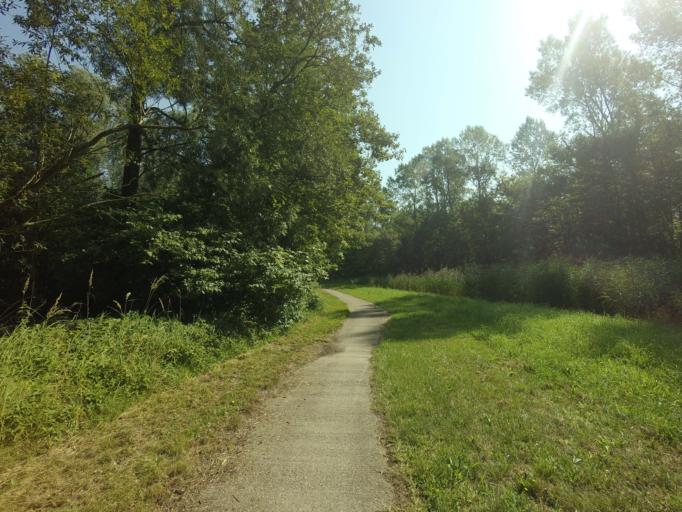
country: NL
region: Groningen
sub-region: Gemeente De Marne
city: Ulrum
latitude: 53.3907
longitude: 6.2595
